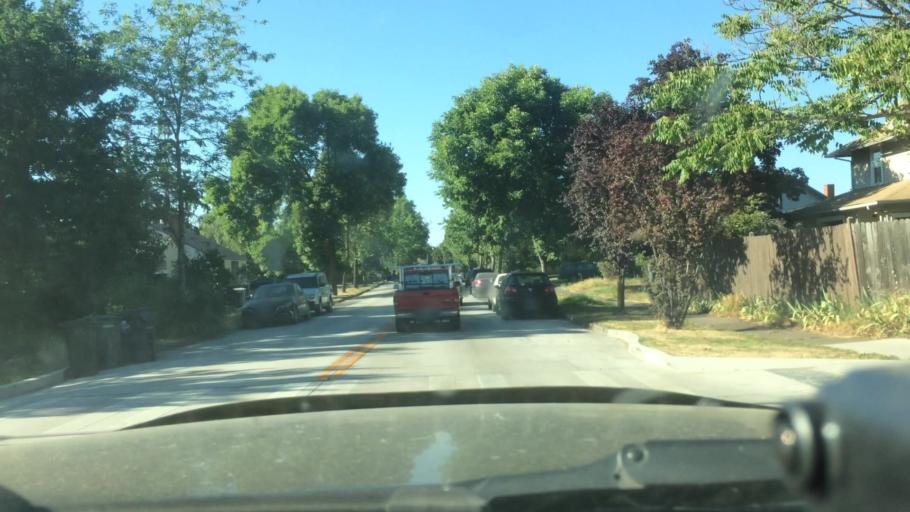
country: US
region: Oregon
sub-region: Lane County
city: Eugene
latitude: 44.0433
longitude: -123.1013
